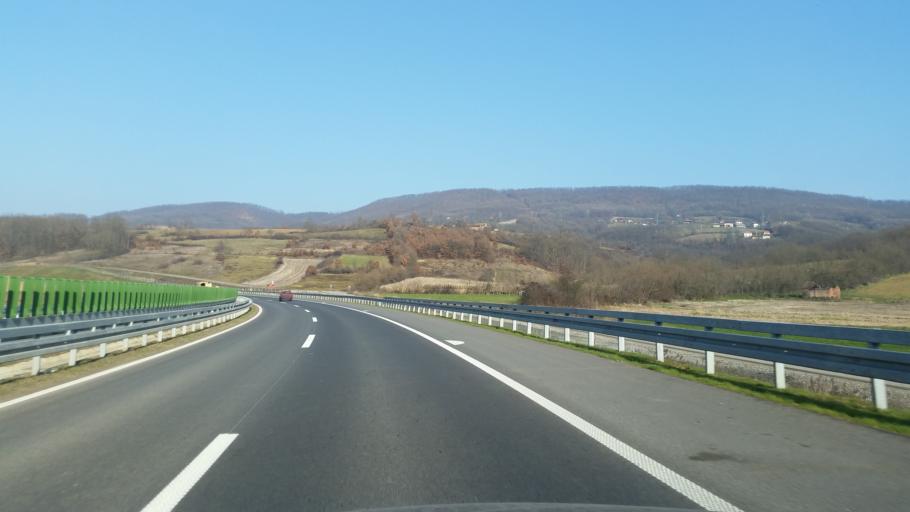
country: RS
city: Prislonica
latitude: 43.9960
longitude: 20.4033
